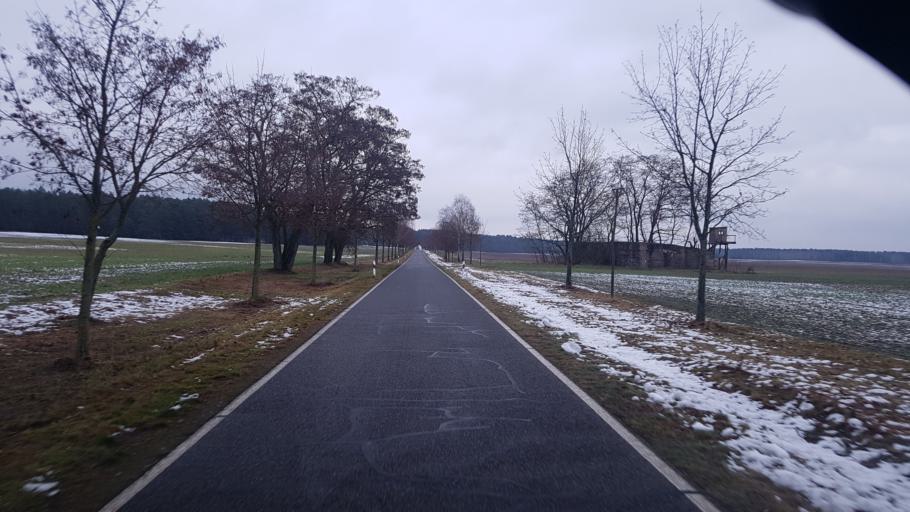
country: DE
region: Brandenburg
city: Jamlitz
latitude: 52.0180
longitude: 14.4262
